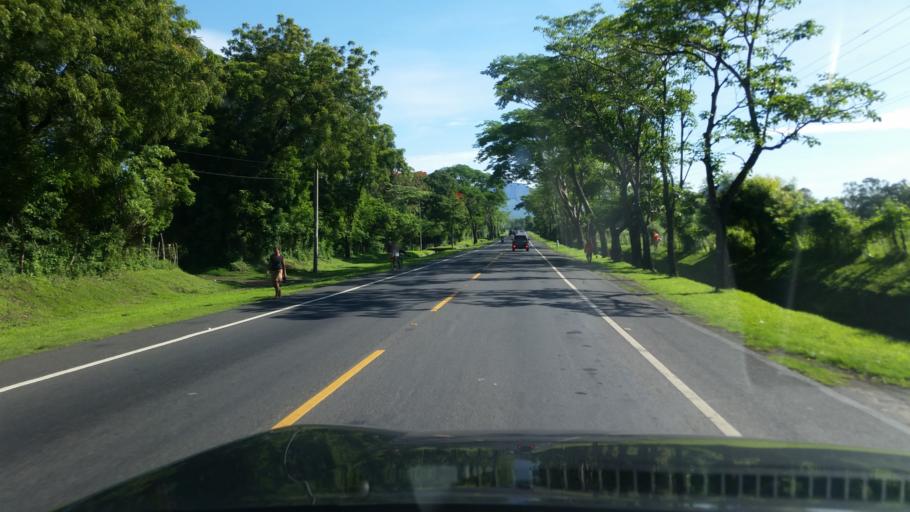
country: NI
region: Leon
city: Telica
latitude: 12.4796
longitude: -86.8624
